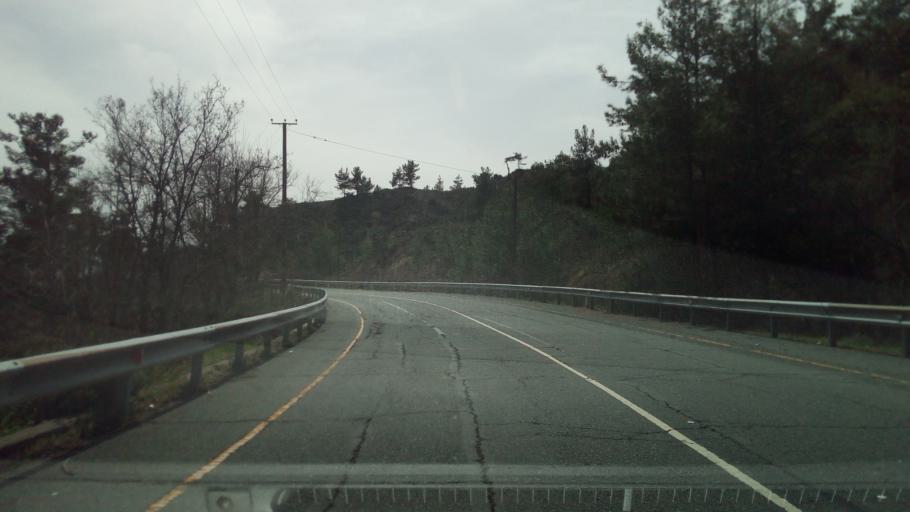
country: CY
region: Limassol
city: Pelendri
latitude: 34.8827
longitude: 32.9461
